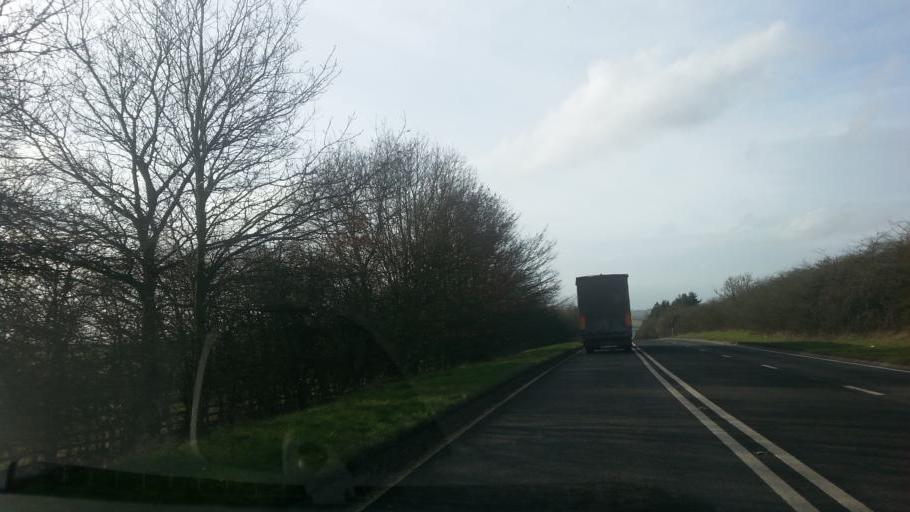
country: GB
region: England
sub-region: District of Rutland
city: Ridlington
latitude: 52.5956
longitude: -0.7632
